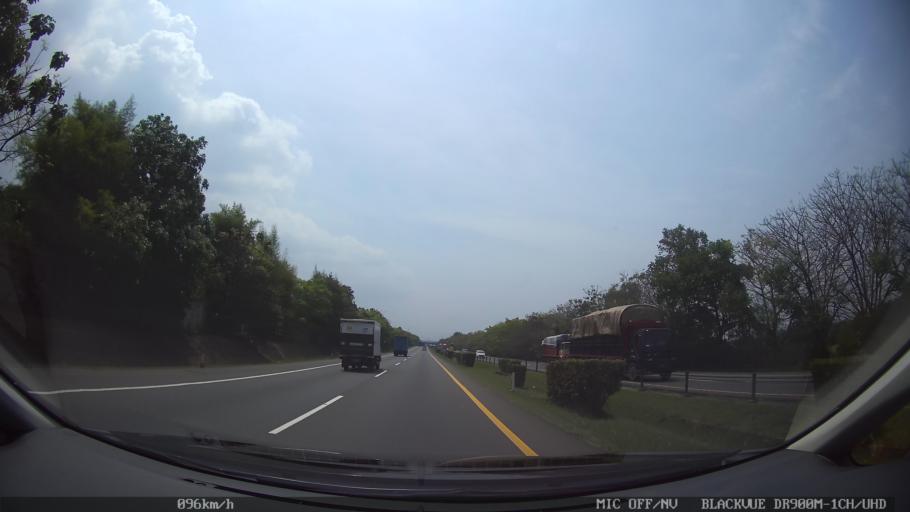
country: ID
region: Banten
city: Serang
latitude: -6.0696
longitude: 106.1276
